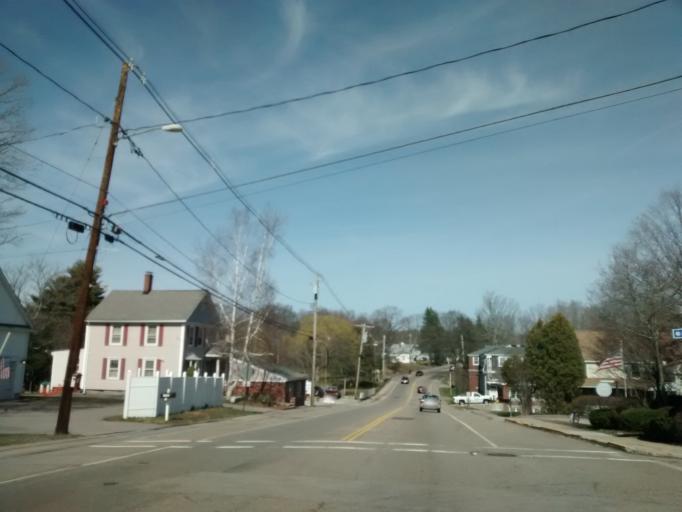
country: US
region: Massachusetts
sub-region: Norfolk County
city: Medway
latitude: 42.1462
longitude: -71.4285
